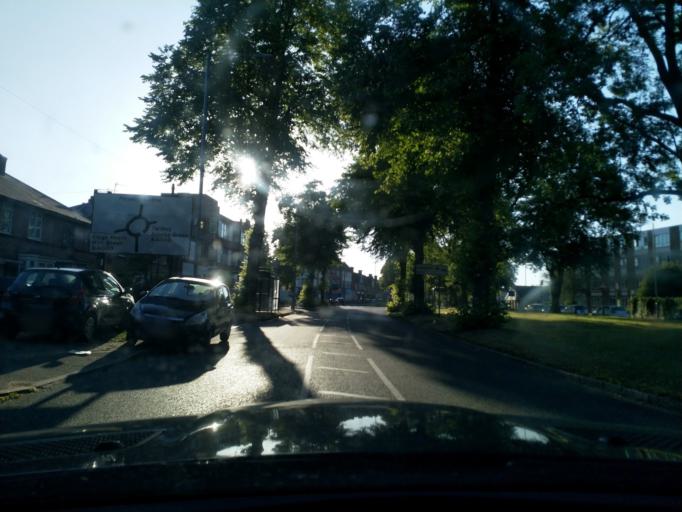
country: GB
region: England
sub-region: City and Borough of Birmingham
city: Acocks Green
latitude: 52.4426
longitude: -1.8319
